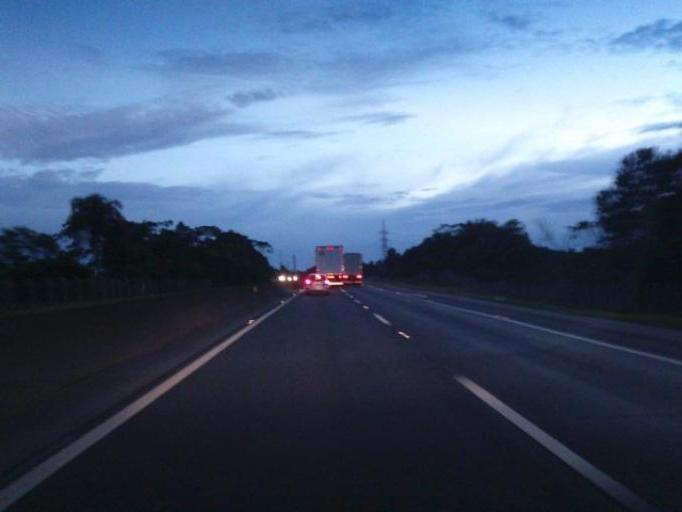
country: BR
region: Santa Catarina
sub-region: Barra Velha
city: Barra Velha
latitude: -26.4904
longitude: -48.7340
